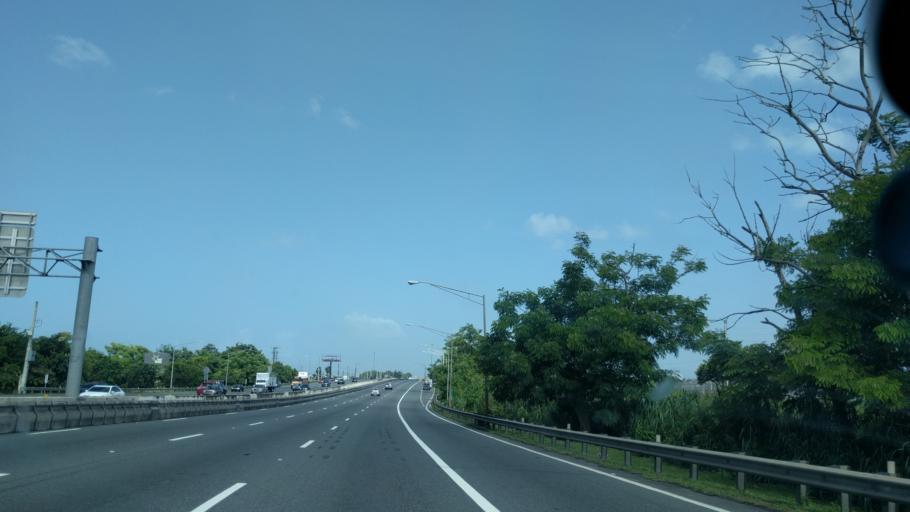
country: PR
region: Bayamon
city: Bayamon
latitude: 18.4224
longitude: -66.1515
